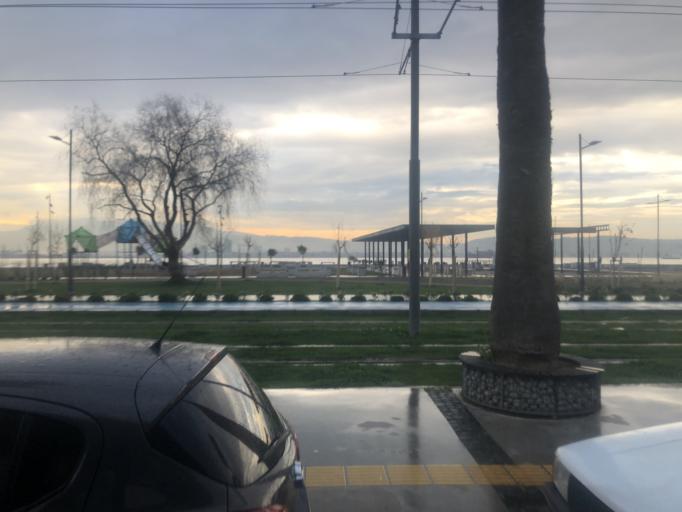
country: TR
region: Izmir
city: Karsiyaka
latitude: 38.4535
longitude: 27.1174
